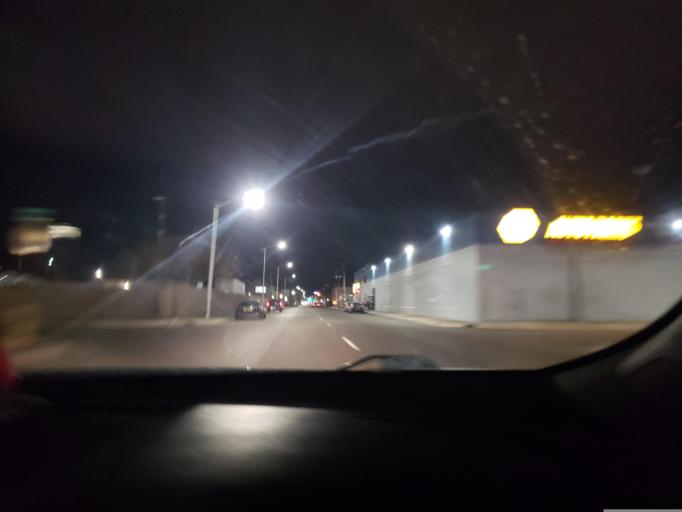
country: US
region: New Mexico
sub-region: Bernalillo County
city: Albuquerque
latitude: 35.0982
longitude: -106.6466
